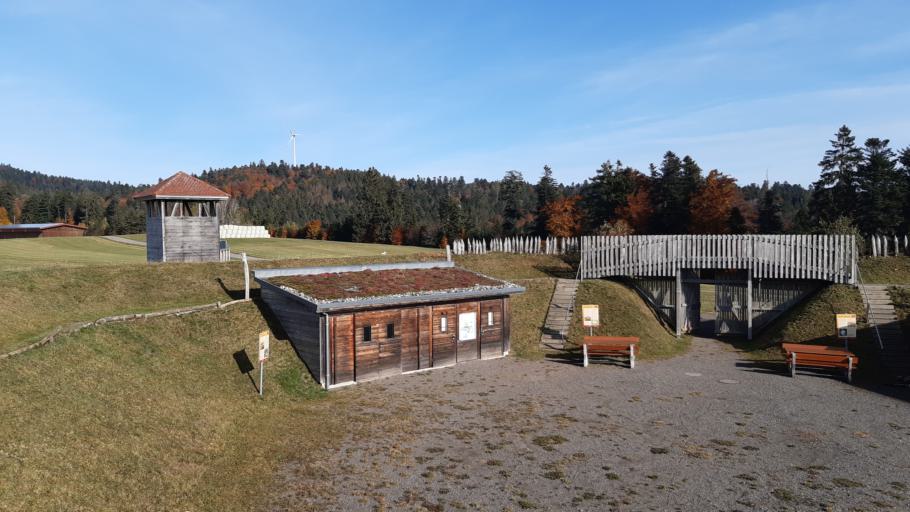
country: DE
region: Baden-Wuerttemberg
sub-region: Freiburg Region
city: Herrischried
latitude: 47.6992
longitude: 7.9489
